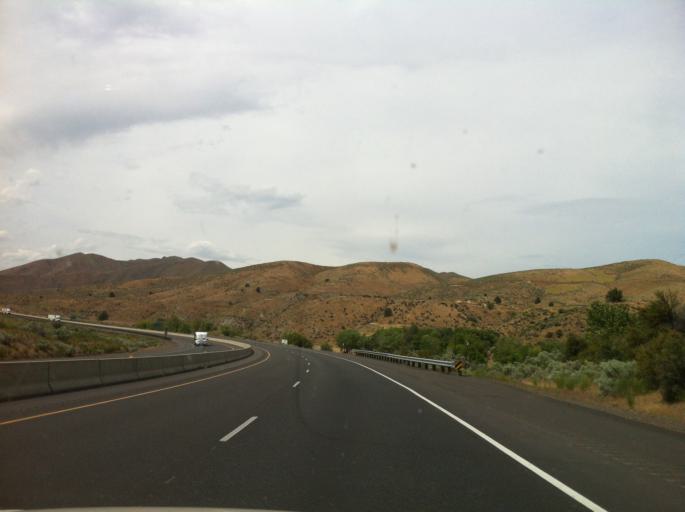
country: US
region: Idaho
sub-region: Washington County
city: Weiser
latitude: 44.4203
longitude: -117.3101
